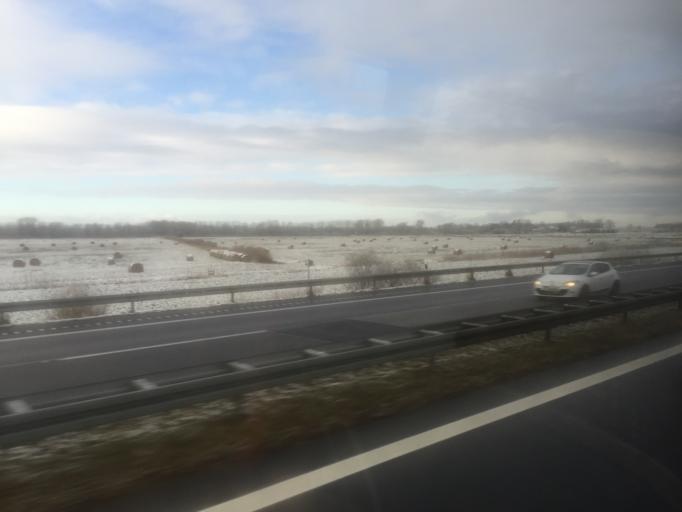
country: DE
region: Brandenburg
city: Fehrbellin
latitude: 52.8284
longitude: 12.7936
